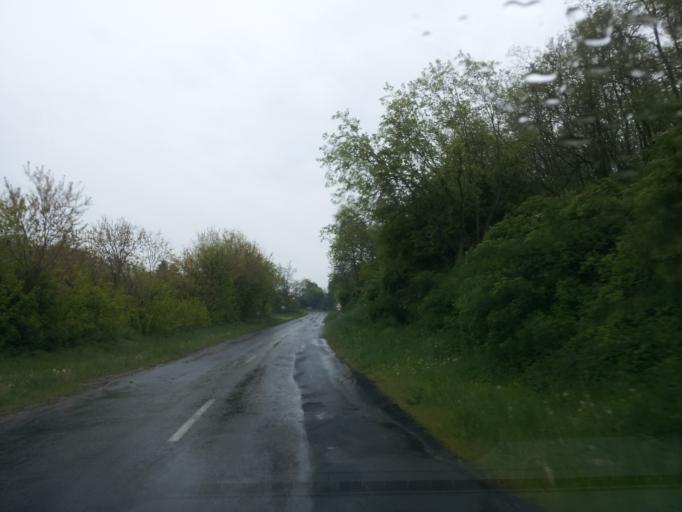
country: HU
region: Tolna
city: Szekszard
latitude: 46.2888
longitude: 18.6699
